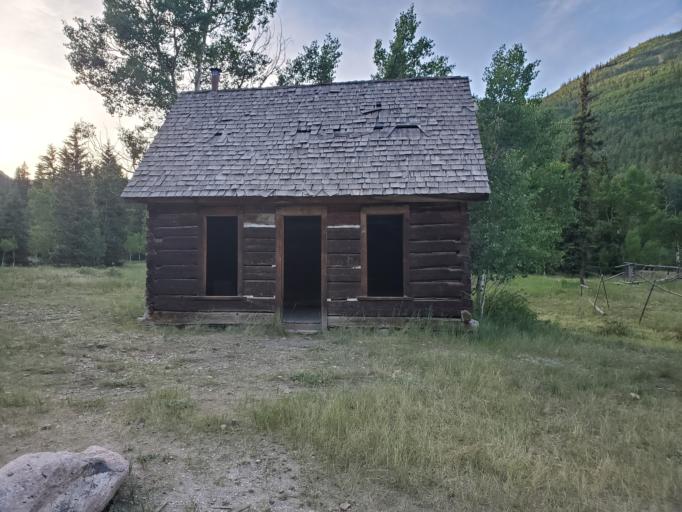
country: US
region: Colorado
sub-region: Hinsdale County
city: Lake City
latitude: 38.0062
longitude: -107.4672
